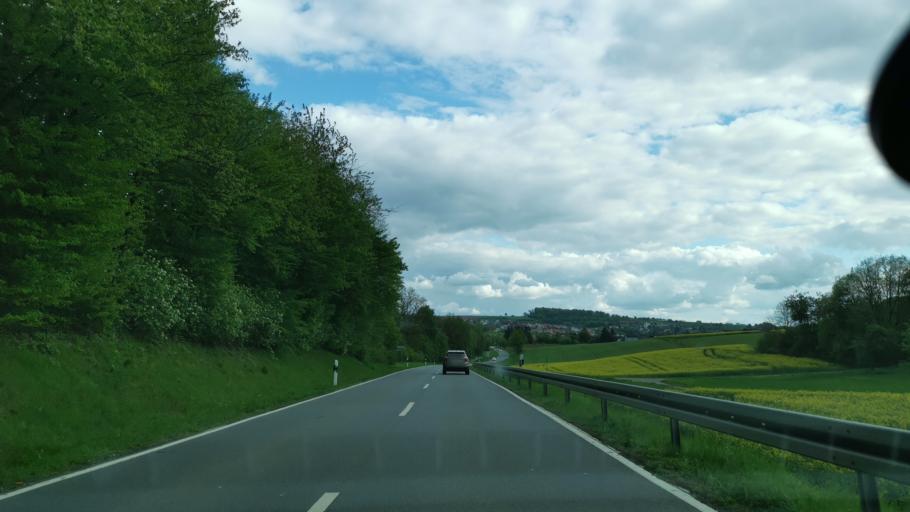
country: DE
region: Baden-Wuerttemberg
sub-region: Karlsruhe Region
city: Osterburken
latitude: 49.4443
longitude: 9.4273
